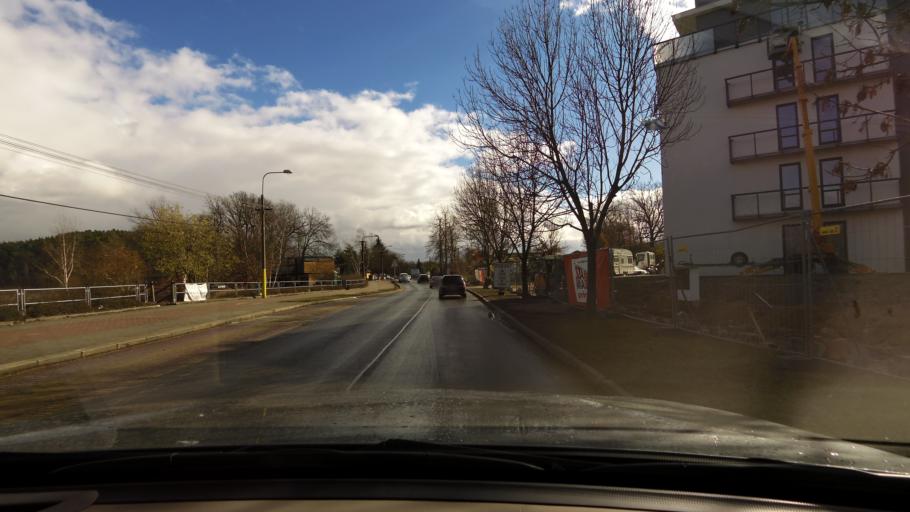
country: CZ
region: Plzensky
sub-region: Okres Plzen-Mesto
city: Pilsen
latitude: 49.7712
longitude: 13.3972
